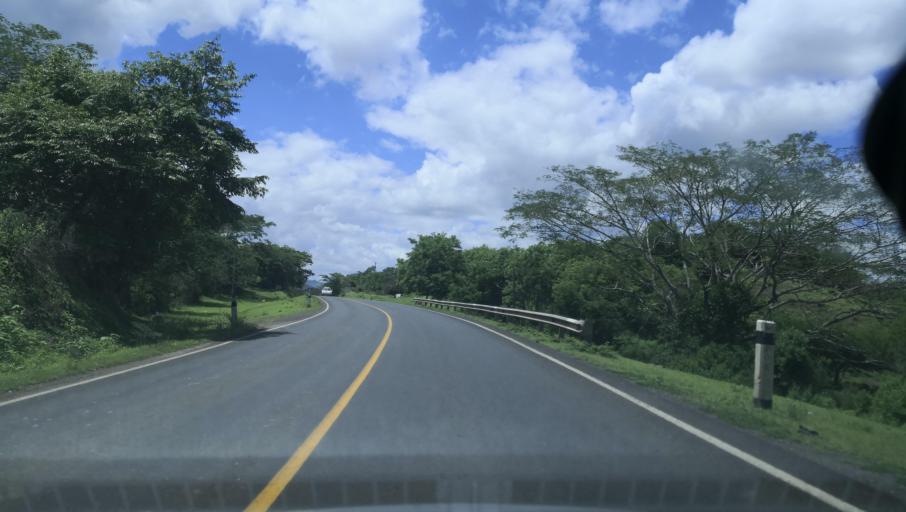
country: NI
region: Esteli
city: Condega
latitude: 13.3955
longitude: -86.3998
